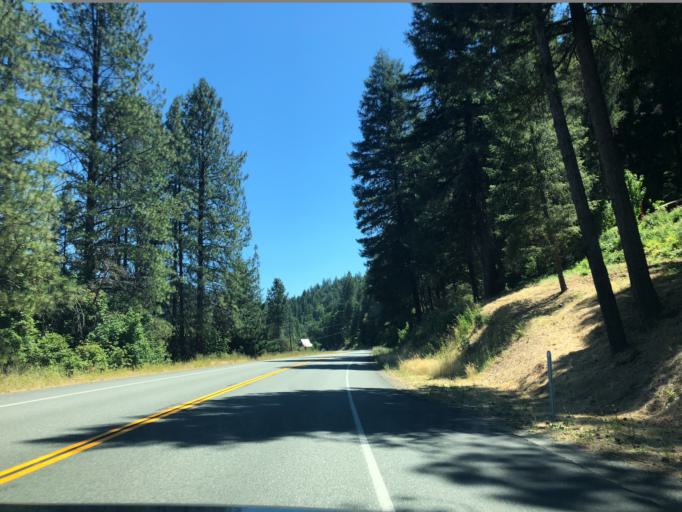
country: US
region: California
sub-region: Trinity County
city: Weaverville
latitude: 40.6544
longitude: -122.9293
